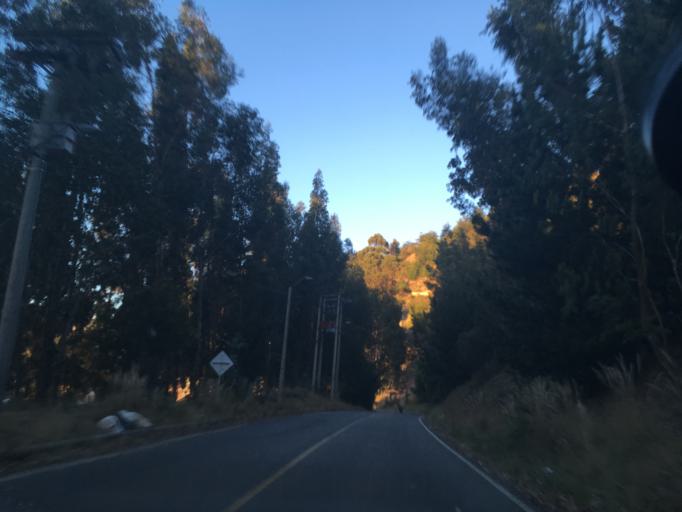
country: CO
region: Boyaca
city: Aquitania
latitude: 5.5442
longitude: -72.8844
